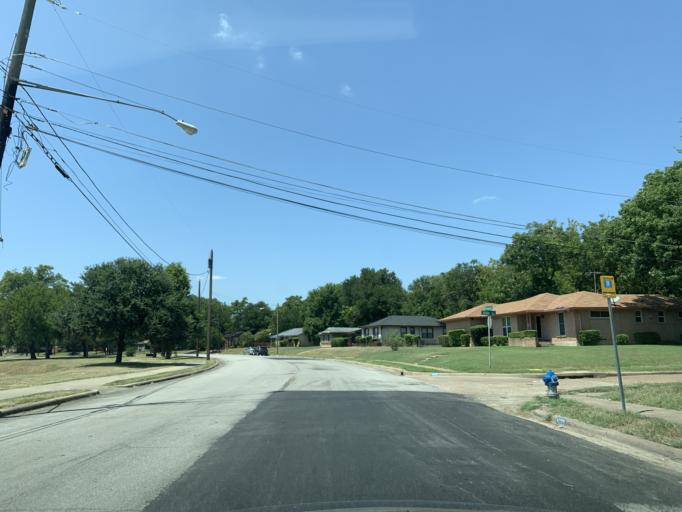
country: US
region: Texas
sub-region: Dallas County
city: Cockrell Hill
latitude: 32.6862
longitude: -96.8094
